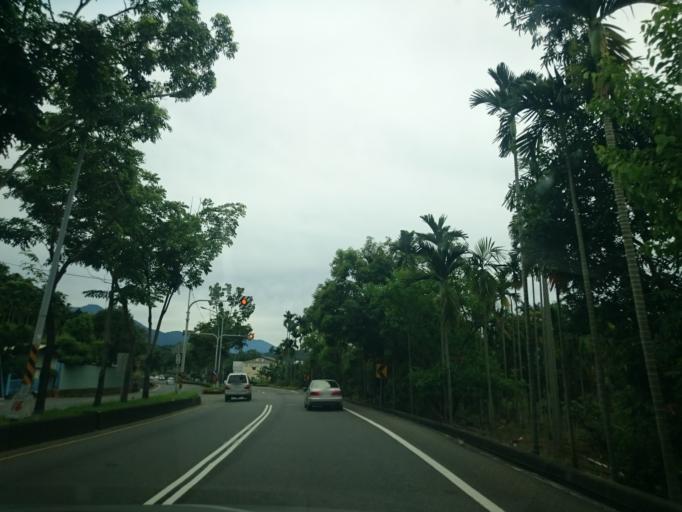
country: TW
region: Taiwan
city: Lugu
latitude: 23.8322
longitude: 120.7385
